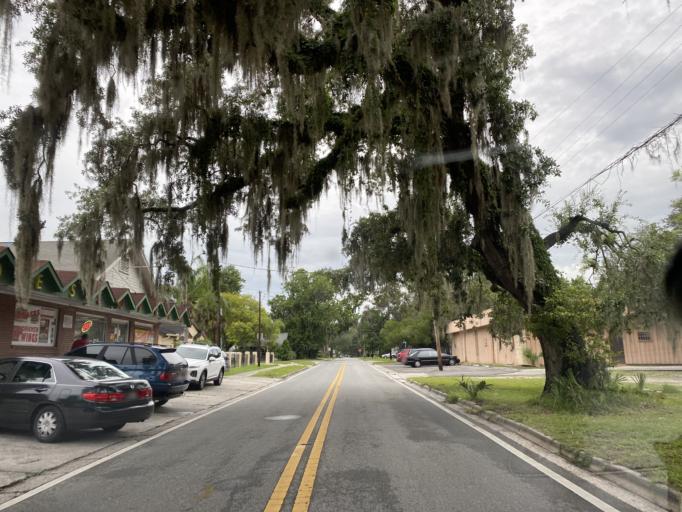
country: US
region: Florida
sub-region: Seminole County
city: Sanford
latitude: 28.8063
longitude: -81.2630
